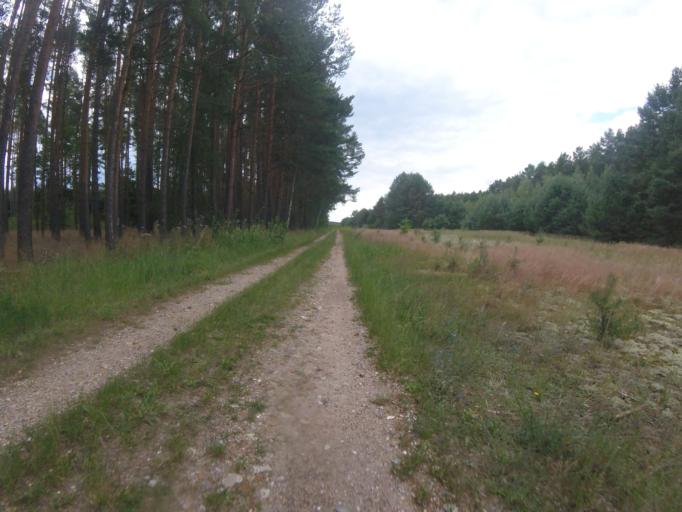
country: DE
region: Brandenburg
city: Bestensee
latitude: 52.2851
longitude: 13.7335
